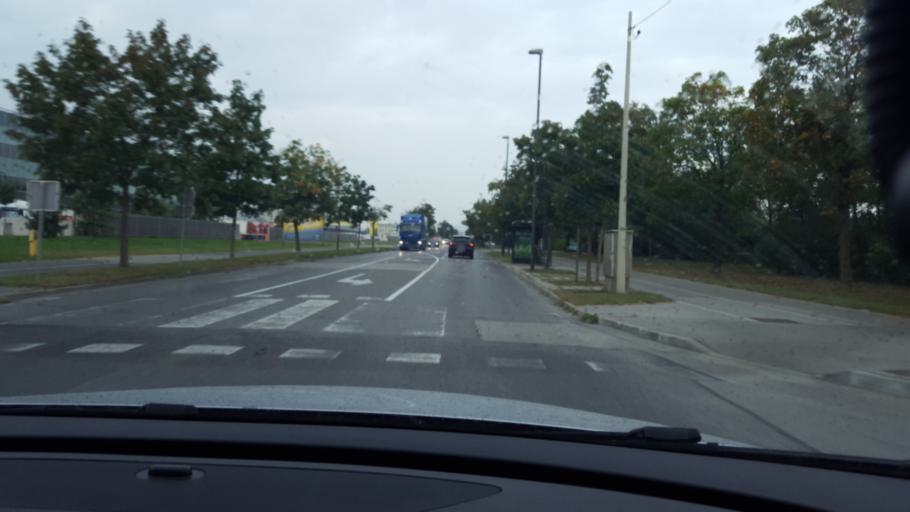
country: SI
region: Dol pri Ljubljani
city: Dol pri Ljubljani
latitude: 46.0622
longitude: 14.5670
